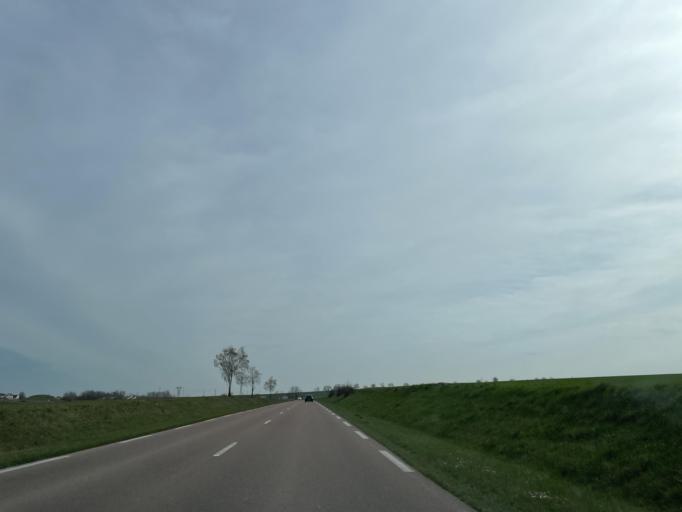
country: FR
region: Champagne-Ardenne
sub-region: Departement de l'Aube
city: Nogent-sur-Seine
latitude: 48.4828
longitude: 3.5067
